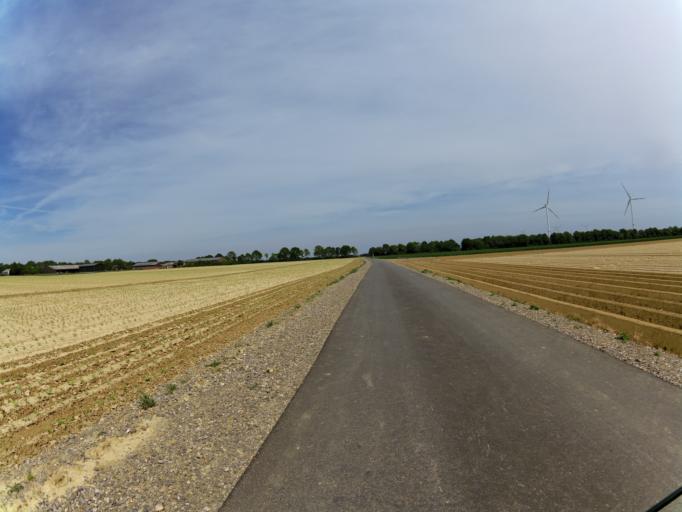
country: DE
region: North Rhine-Westphalia
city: Siersdorf
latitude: 50.8706
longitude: 6.2384
